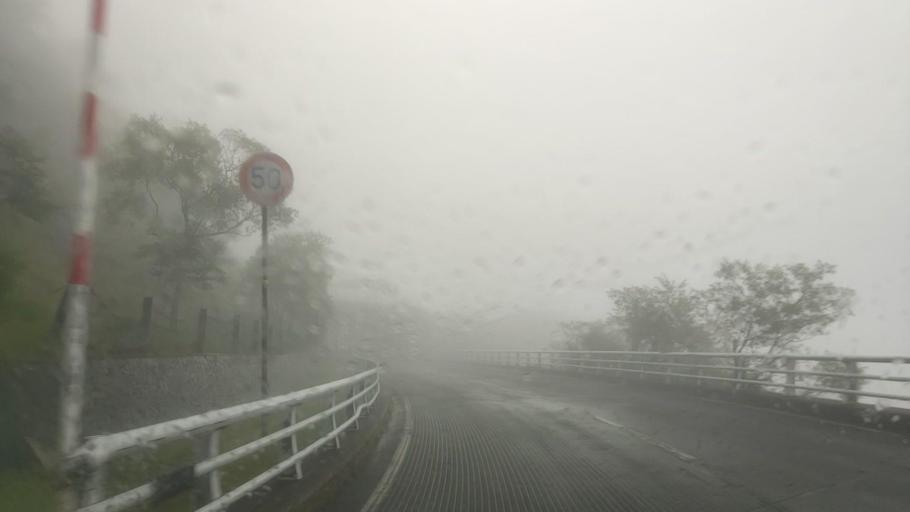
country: JP
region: Hokkaido
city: Date
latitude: 42.5495
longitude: 141.0849
